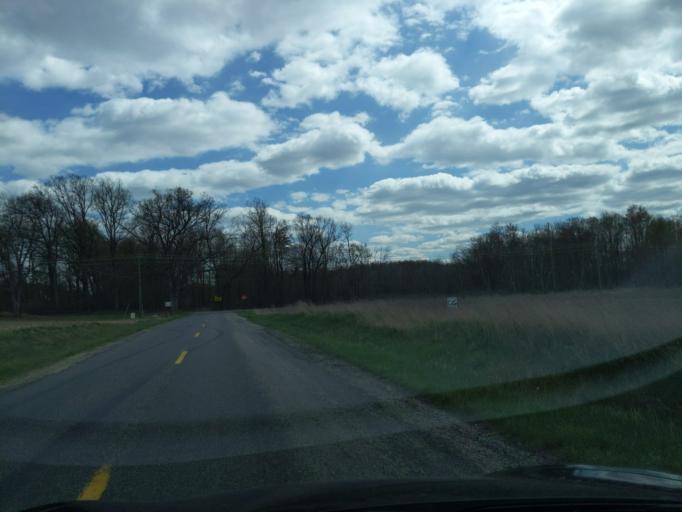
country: US
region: Michigan
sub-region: Eaton County
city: Eaton Rapids
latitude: 42.5105
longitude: -84.5420
